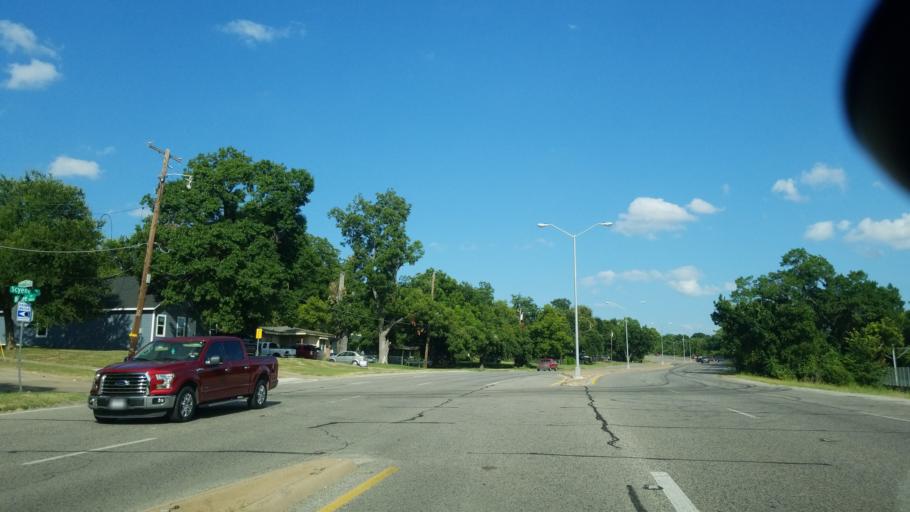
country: US
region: Texas
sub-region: Dallas County
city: Dallas
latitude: 32.7653
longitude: -96.7152
